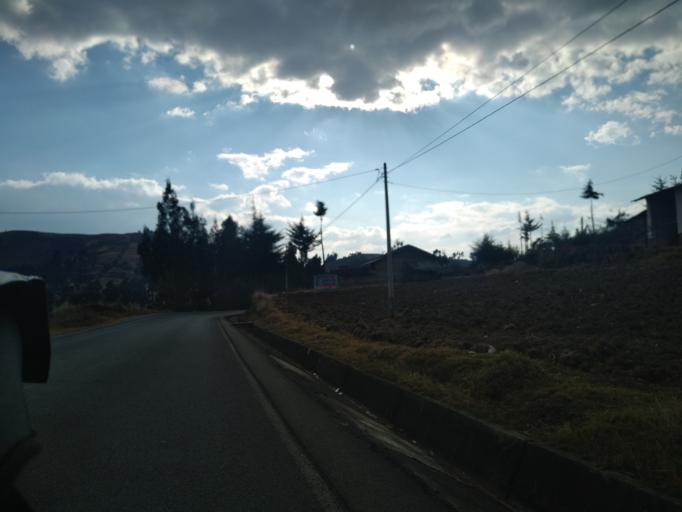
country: PE
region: Cajamarca
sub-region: Provincia de Cajamarca
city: Llacanora
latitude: -7.1435
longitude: -78.4044
